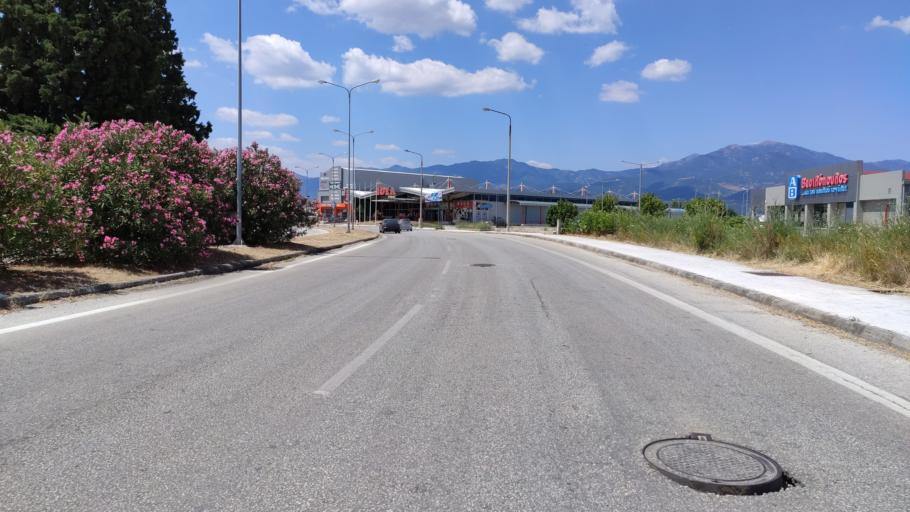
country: GR
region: East Macedonia and Thrace
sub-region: Nomos Rodopis
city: Komotini
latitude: 41.1263
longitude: 25.3917
